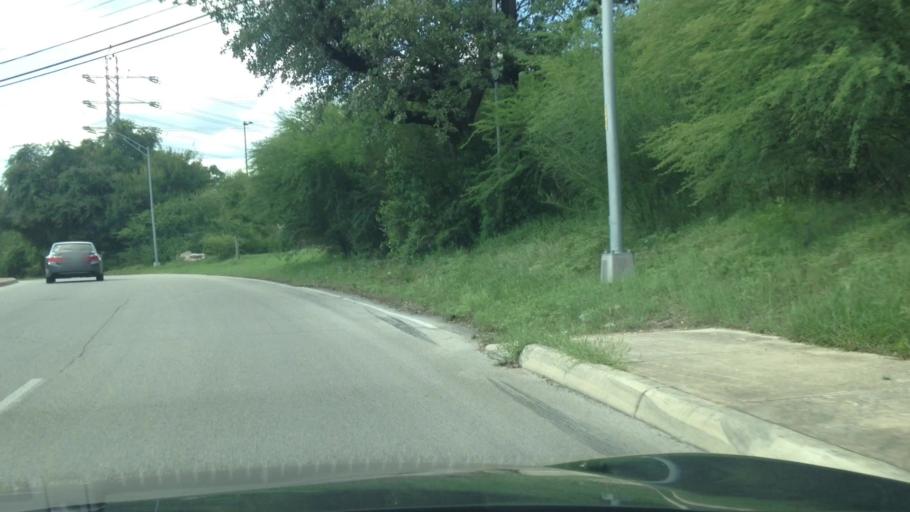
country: US
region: Texas
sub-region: Bexar County
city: Shavano Park
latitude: 29.5434
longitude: -98.5869
